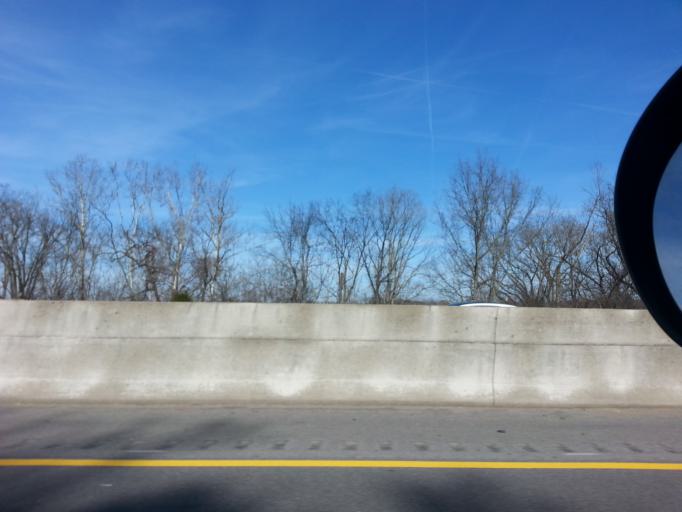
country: US
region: Tennessee
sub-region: Davidson County
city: Oak Hill
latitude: 36.0659
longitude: -86.6859
